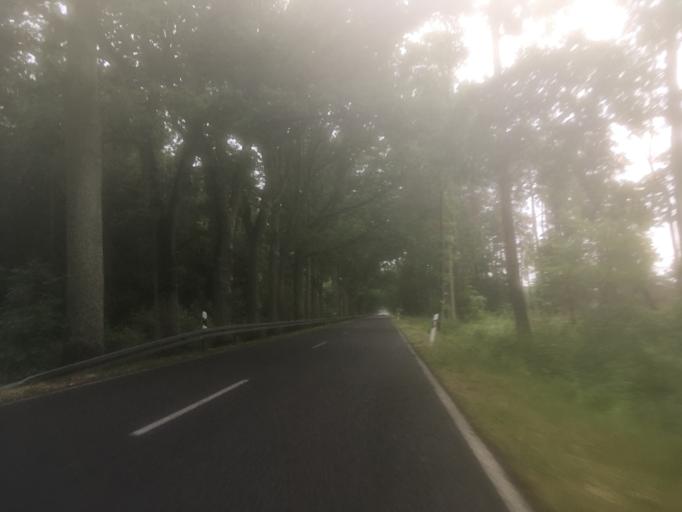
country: DE
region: Brandenburg
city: Zehdenick
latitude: 53.0342
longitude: 13.3280
